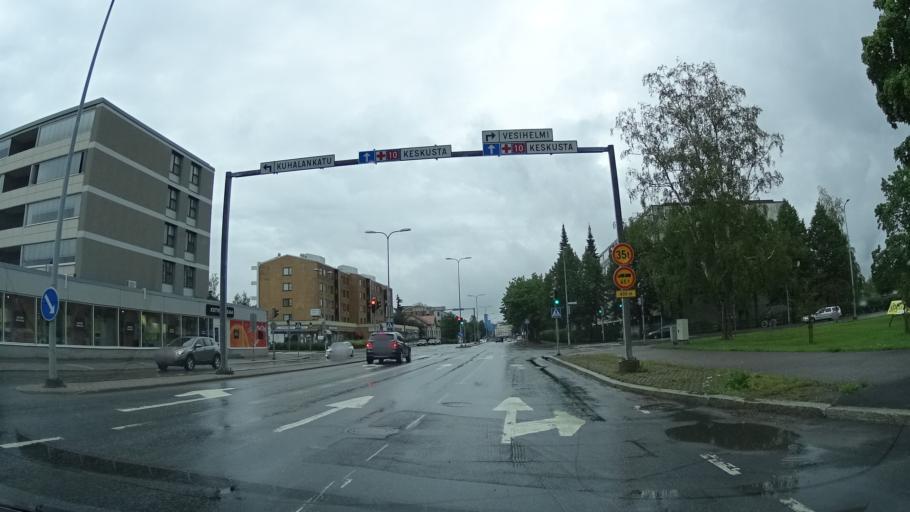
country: FI
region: Haeme
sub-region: Forssa
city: Forssa
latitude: 60.8111
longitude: 23.6156
